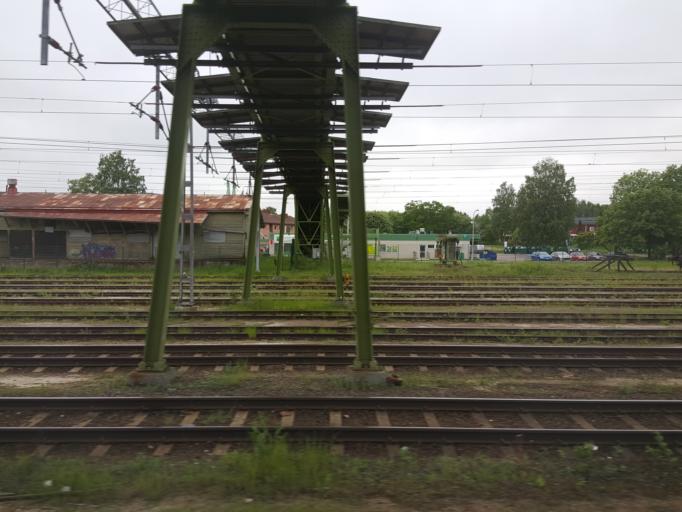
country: SE
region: Dalarna
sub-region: Avesta Kommun
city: Avesta
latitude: 60.1309
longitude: 16.2155
